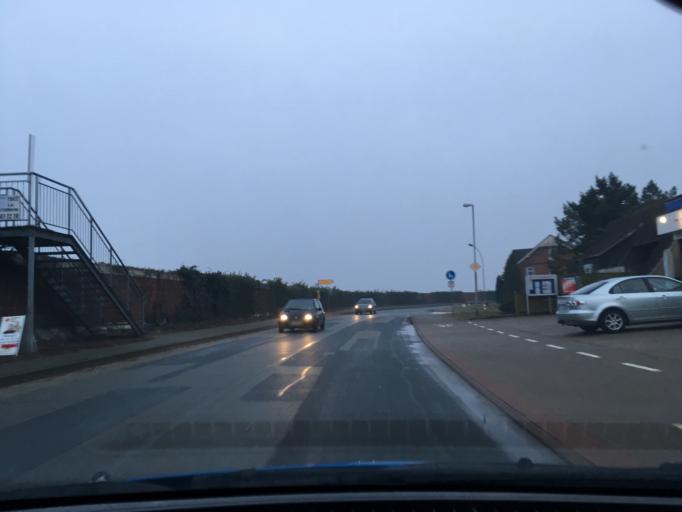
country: DE
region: Lower Saxony
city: Stelle
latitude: 53.4143
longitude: 10.1433
